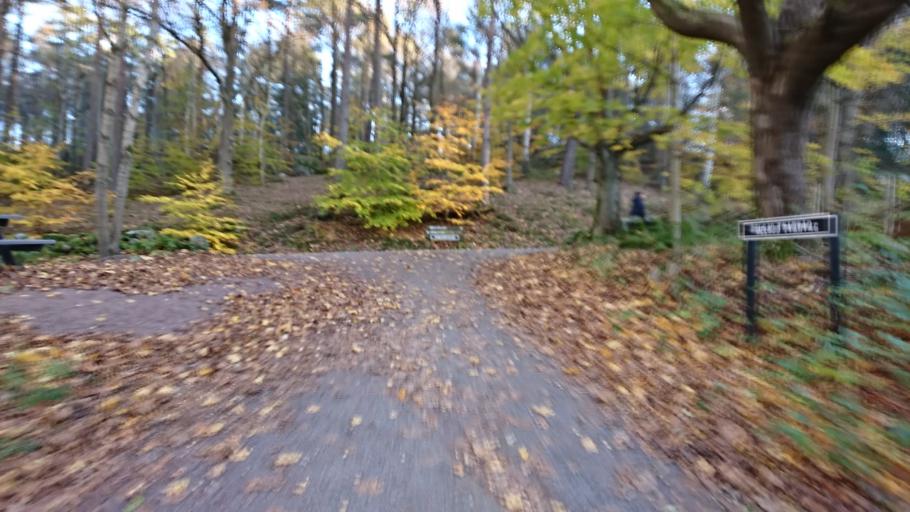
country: SE
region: Vaestra Goetaland
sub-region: Molndal
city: Moelndal
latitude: 57.6908
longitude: 12.0307
